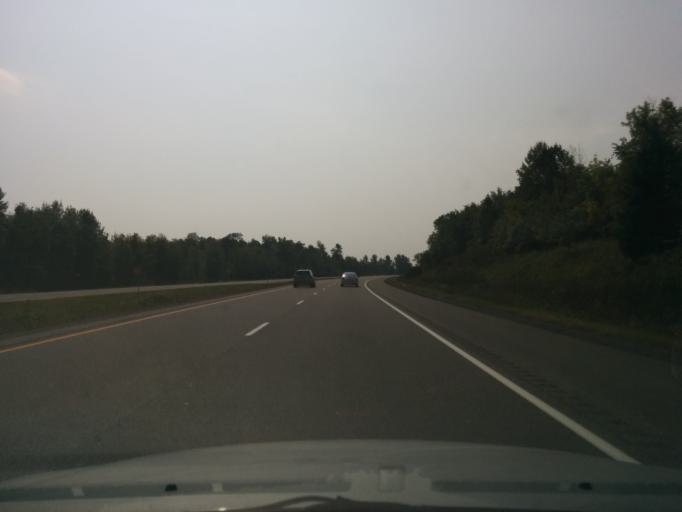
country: CA
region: Ontario
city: Bells Corners
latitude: 45.1340
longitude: -75.6758
